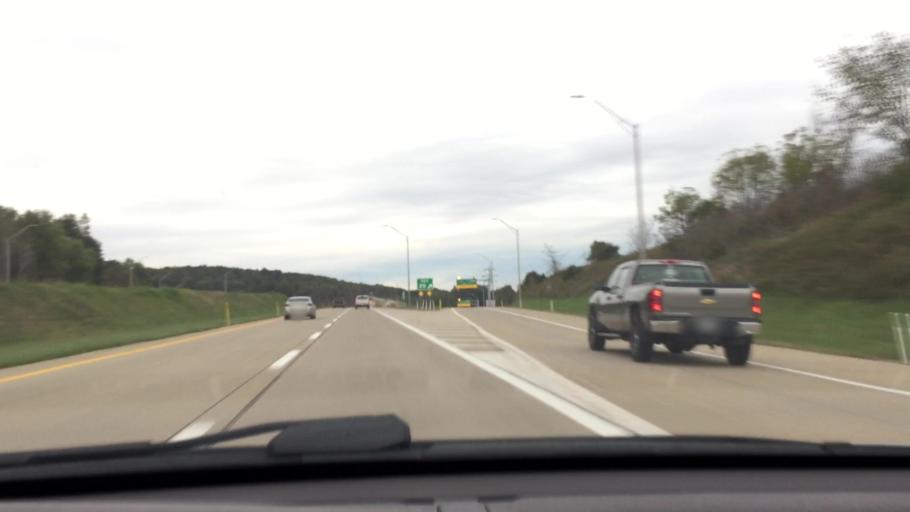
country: US
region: Pennsylvania
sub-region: Lawrence County
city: New Beaver
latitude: 40.9128
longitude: -80.3824
